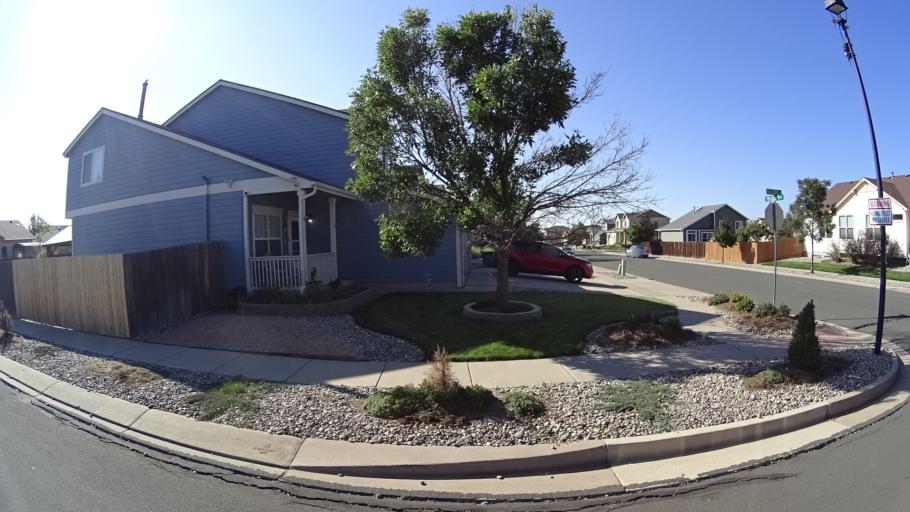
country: US
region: Colorado
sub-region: El Paso County
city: Cimarron Hills
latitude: 38.8918
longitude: -104.6955
